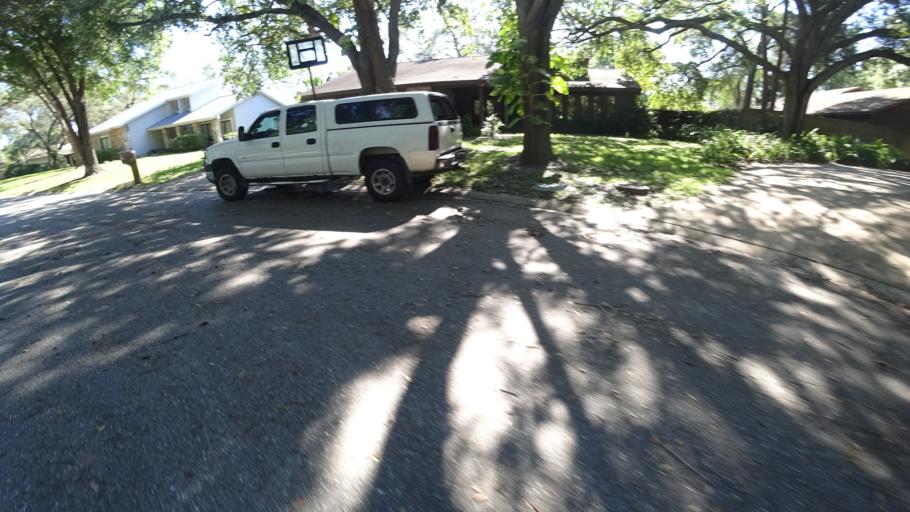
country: US
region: Florida
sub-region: Manatee County
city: West Bradenton
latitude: 27.5003
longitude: -82.6093
